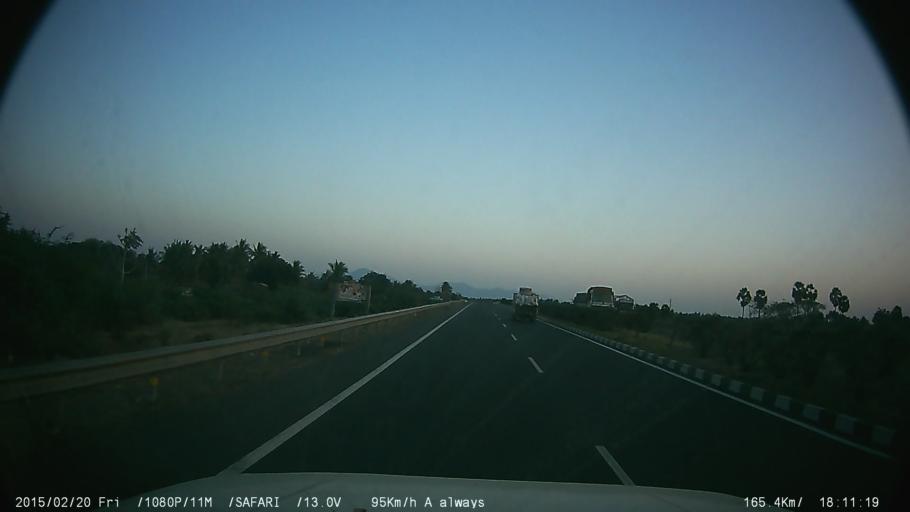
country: IN
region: Tamil Nadu
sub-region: Dharmapuri
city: Palakkodu
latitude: 12.2660
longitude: 78.1964
